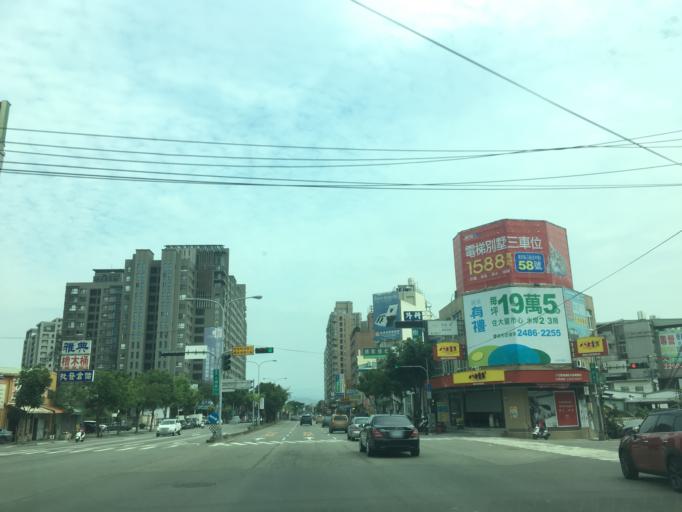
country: TW
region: Taiwan
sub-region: Taichung City
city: Taichung
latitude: 24.1129
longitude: 120.6576
